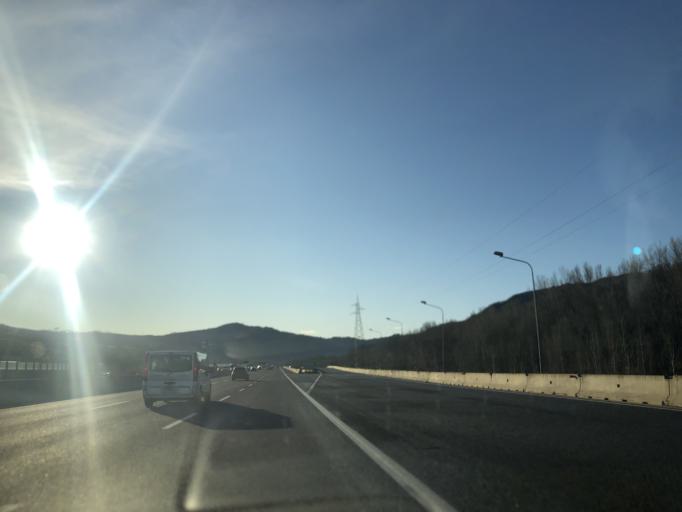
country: IT
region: Emilia-Romagna
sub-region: Provincia di Bologna
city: Sasso Marconi
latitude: 44.3637
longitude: 11.2597
